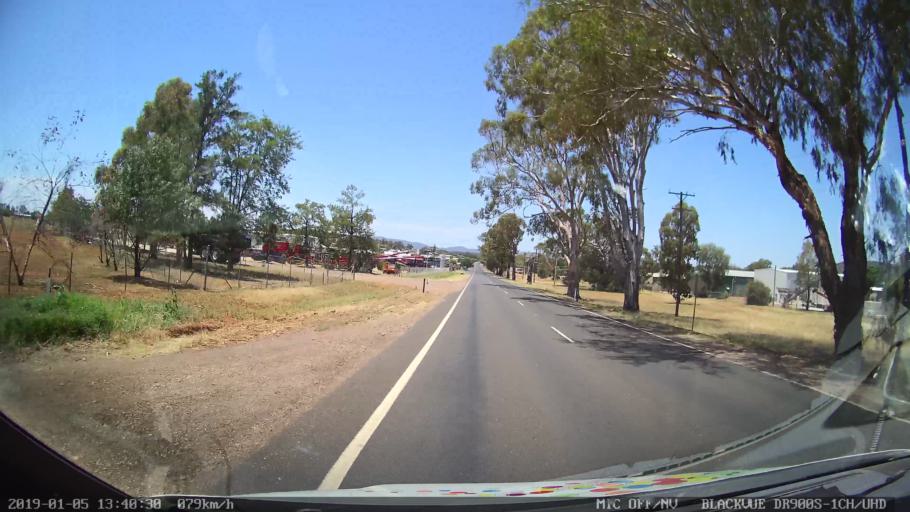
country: AU
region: New South Wales
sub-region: Gunnedah
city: Gunnedah
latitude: -30.9816
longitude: 150.2297
